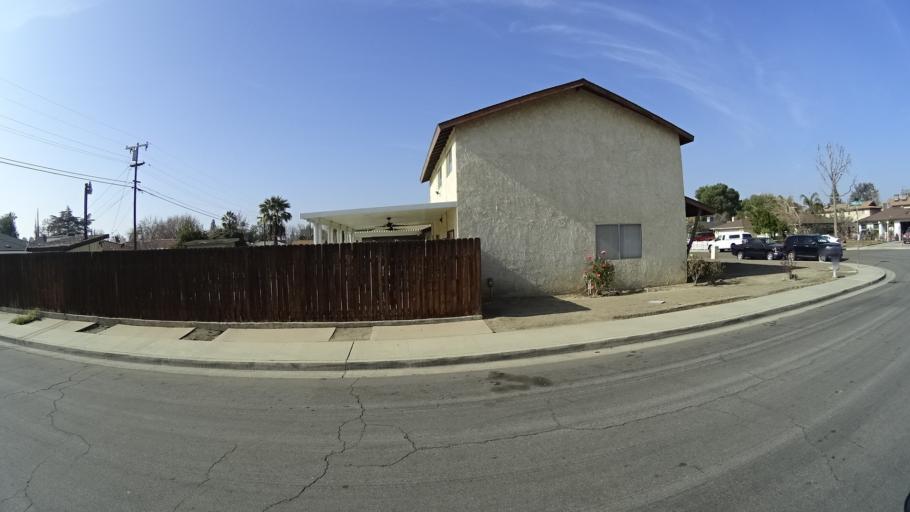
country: US
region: California
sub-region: Kern County
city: Bakersfield
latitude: 35.3287
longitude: -119.0412
